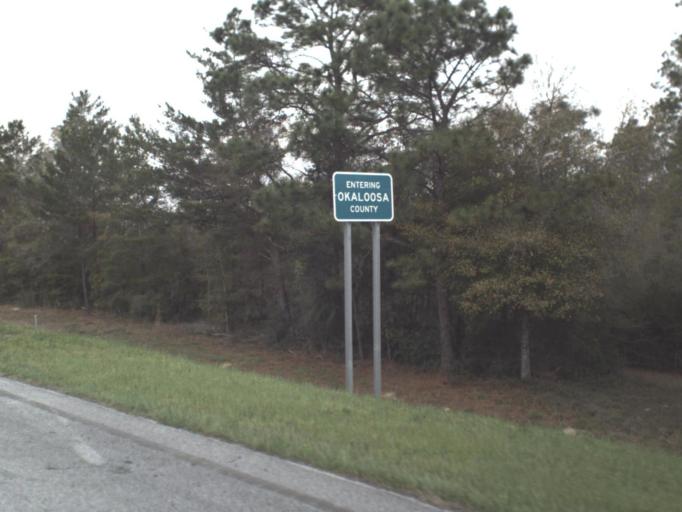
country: US
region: Florida
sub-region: Okaloosa County
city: Crestview
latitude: 30.7296
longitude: -86.3918
